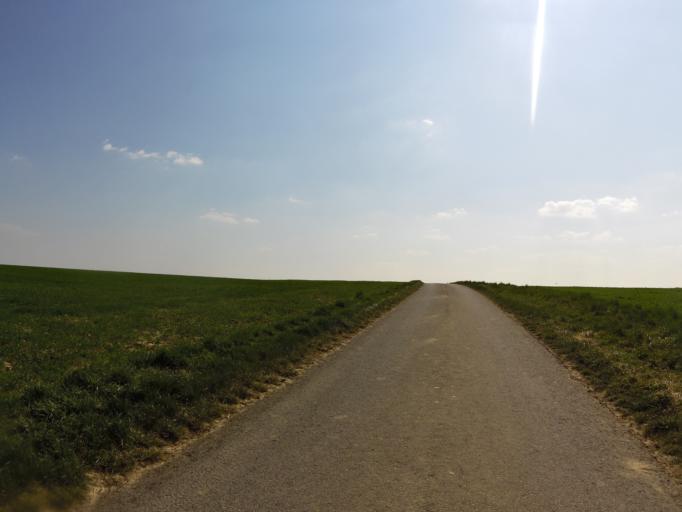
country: DE
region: Bavaria
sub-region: Regierungsbezirk Unterfranken
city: Dettelbach
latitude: 49.8170
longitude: 10.1343
